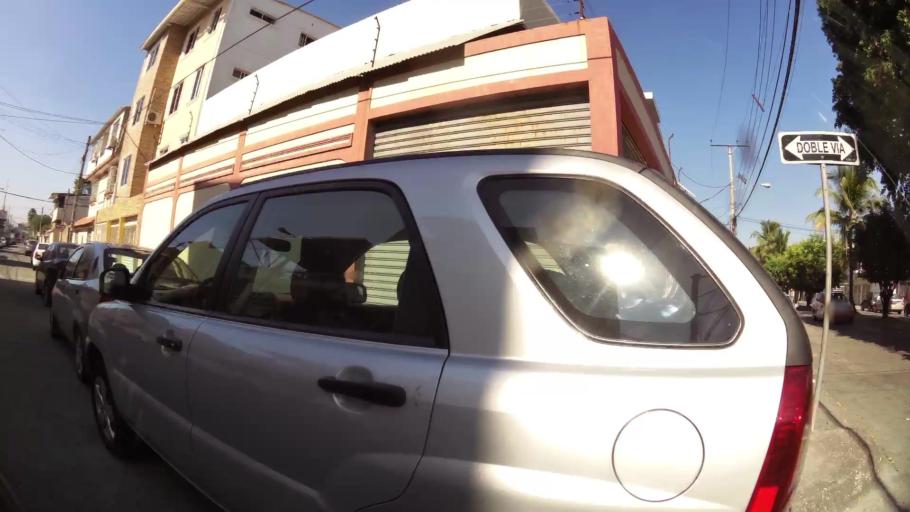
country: EC
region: Guayas
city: Eloy Alfaro
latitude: -2.1447
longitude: -79.9023
